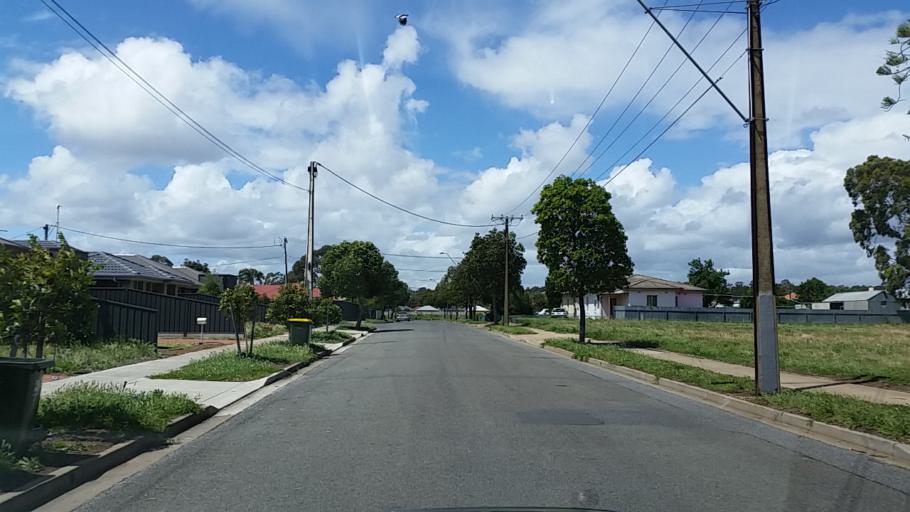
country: AU
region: South Australia
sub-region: Port Adelaide Enfield
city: Enfield
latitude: -34.8508
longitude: 138.5960
